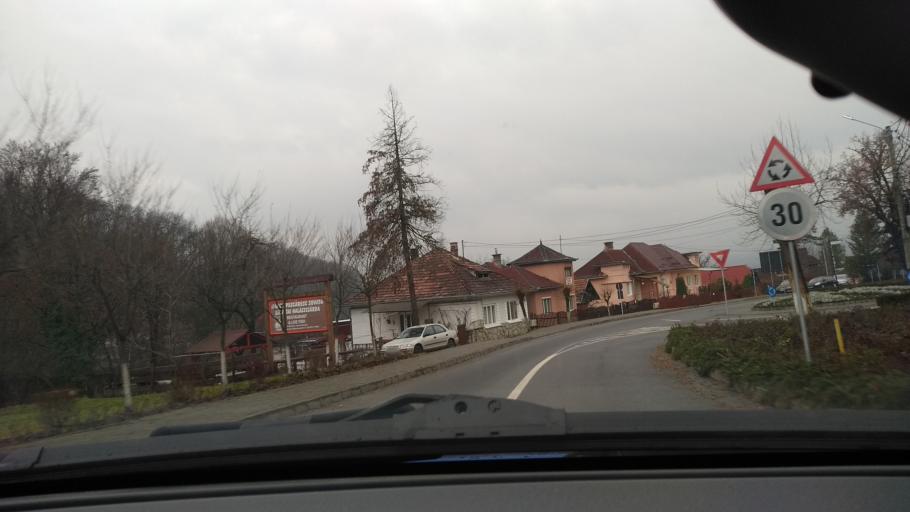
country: RO
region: Mures
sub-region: Oras Sovata
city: Sovata
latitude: 46.5969
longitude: 25.0796
